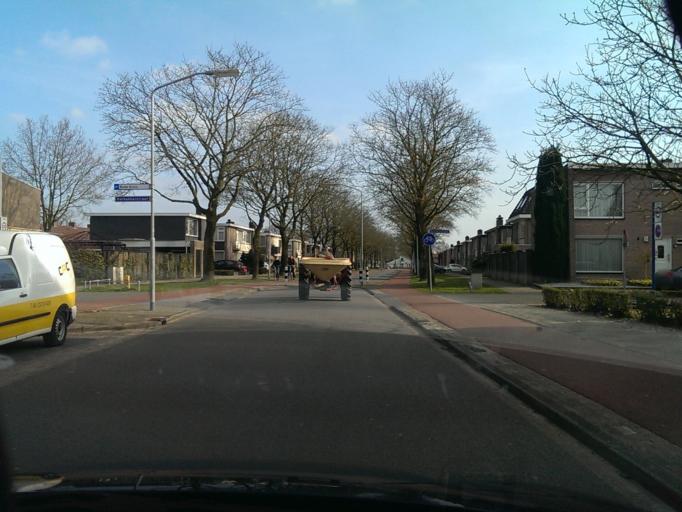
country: NL
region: North Brabant
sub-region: Gemeente Veldhoven
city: Veldhoven
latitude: 51.4072
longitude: 5.4014
